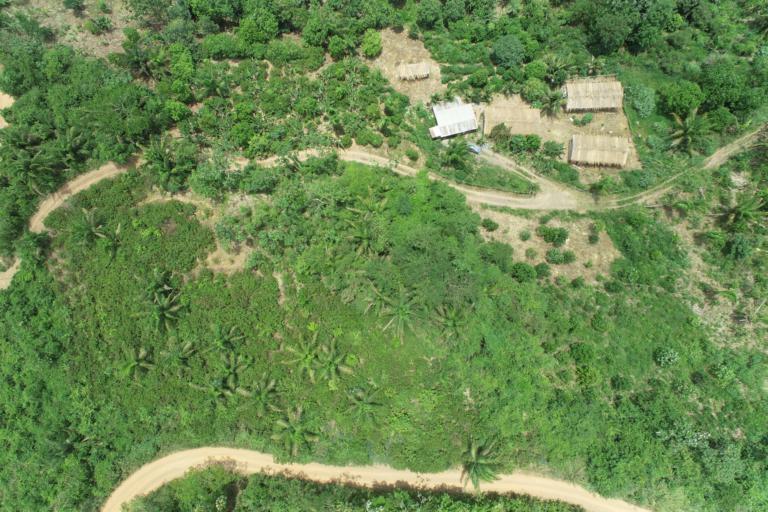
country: BO
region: La Paz
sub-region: Provincia Larecaja
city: Guanay
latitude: -15.7702
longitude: -67.6669
